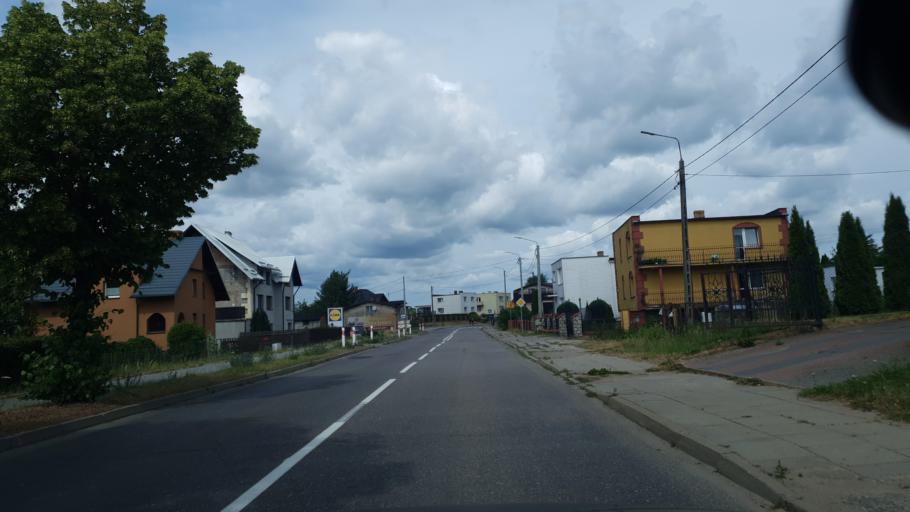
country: PL
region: Pomeranian Voivodeship
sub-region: Powiat kartuski
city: Kartuzy
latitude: 54.3222
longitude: 18.1857
